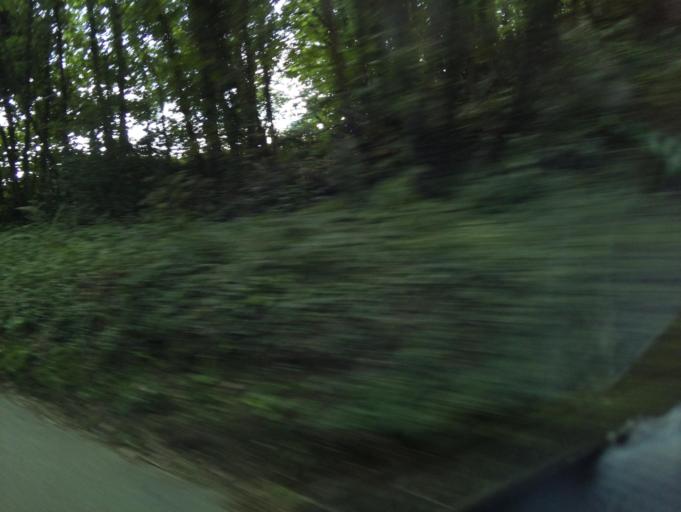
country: GB
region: England
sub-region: Devon
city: South Brent
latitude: 50.4160
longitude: -3.7987
